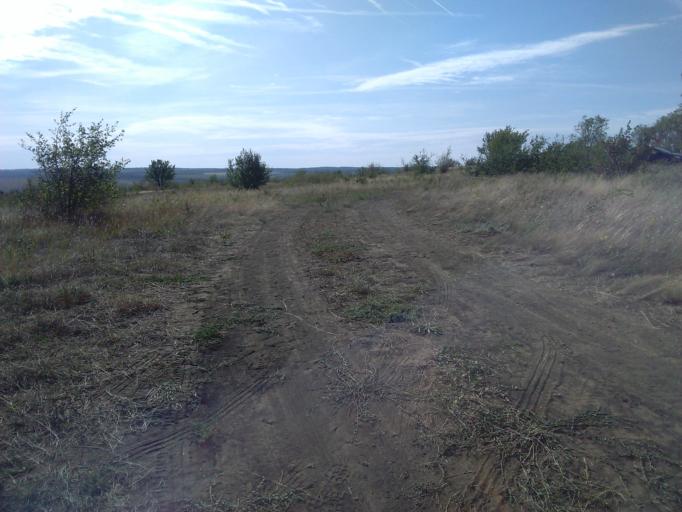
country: RU
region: Rostov
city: Gornyy
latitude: 47.8891
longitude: 40.2410
